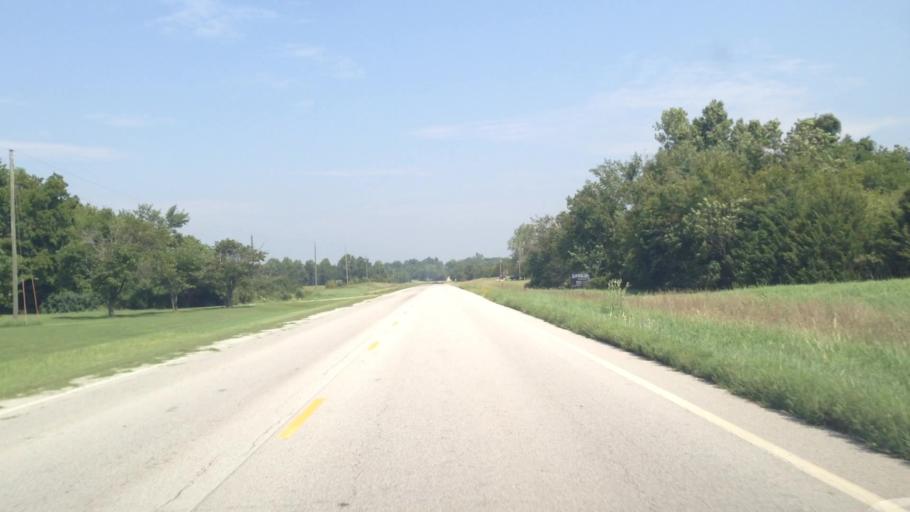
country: US
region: Kansas
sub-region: Labette County
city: Oswego
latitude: 37.1371
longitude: -95.1034
